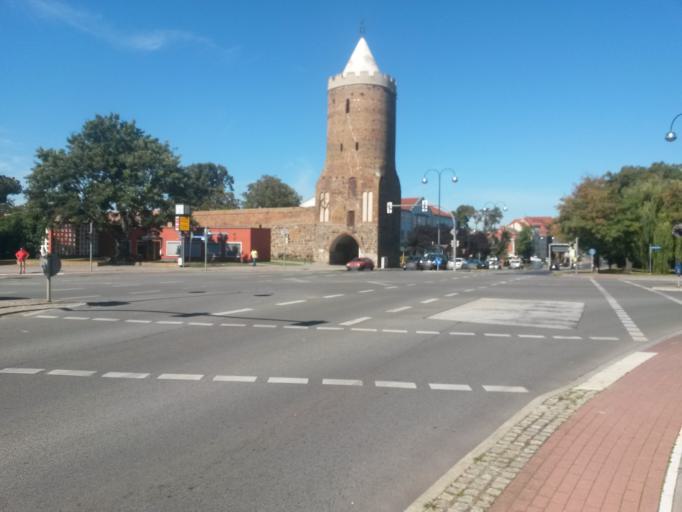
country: DE
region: Brandenburg
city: Prenzlau
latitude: 53.3165
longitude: 13.8623
